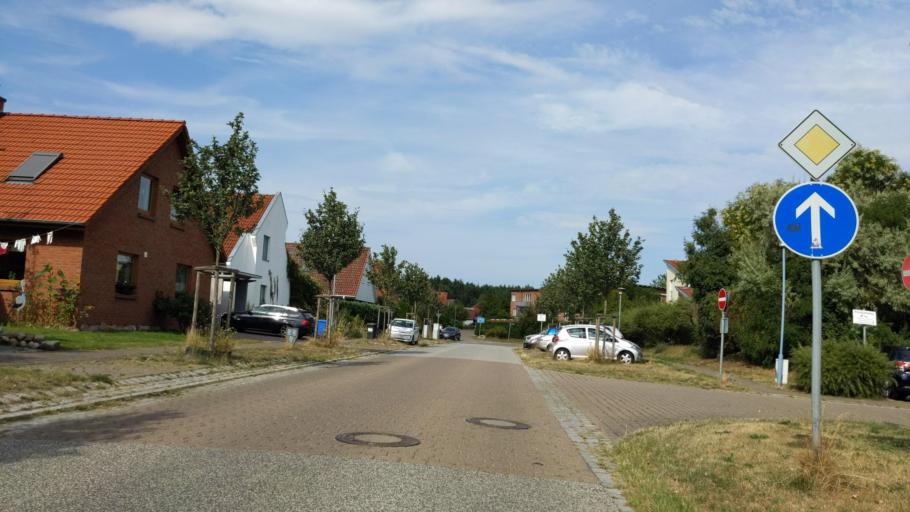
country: DE
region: Schleswig-Holstein
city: Gross Gronau
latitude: 53.8489
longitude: 10.7599
